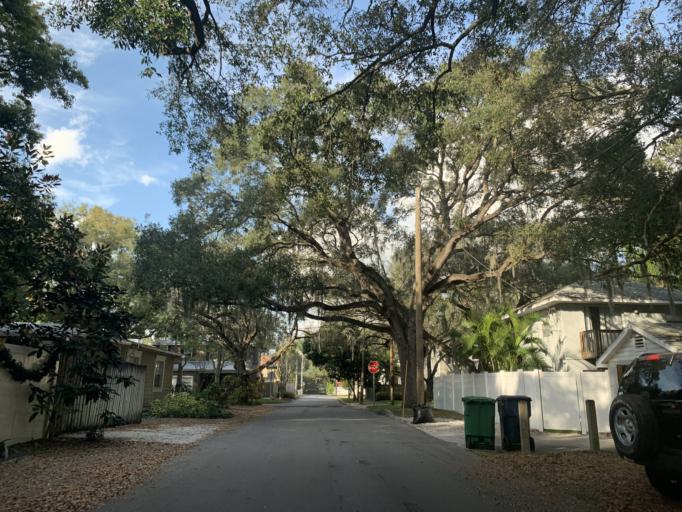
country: US
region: Florida
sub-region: Hillsborough County
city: Tampa
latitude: 27.8957
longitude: -82.4994
